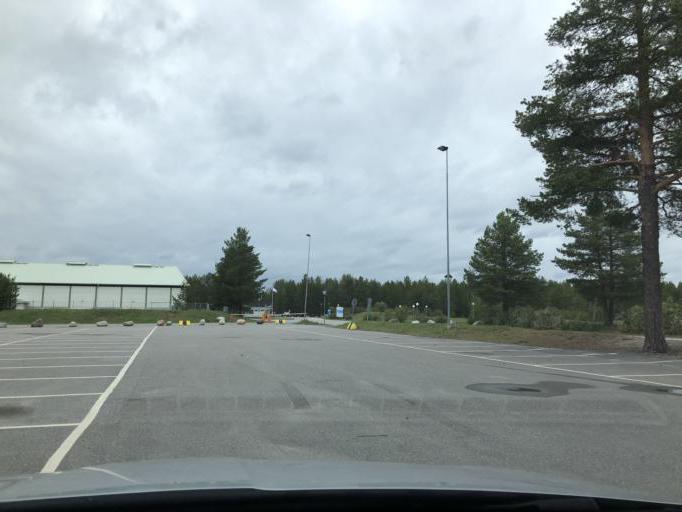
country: SE
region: Norrbotten
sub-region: Pitea Kommun
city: Pitea
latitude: 65.2348
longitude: 21.5310
